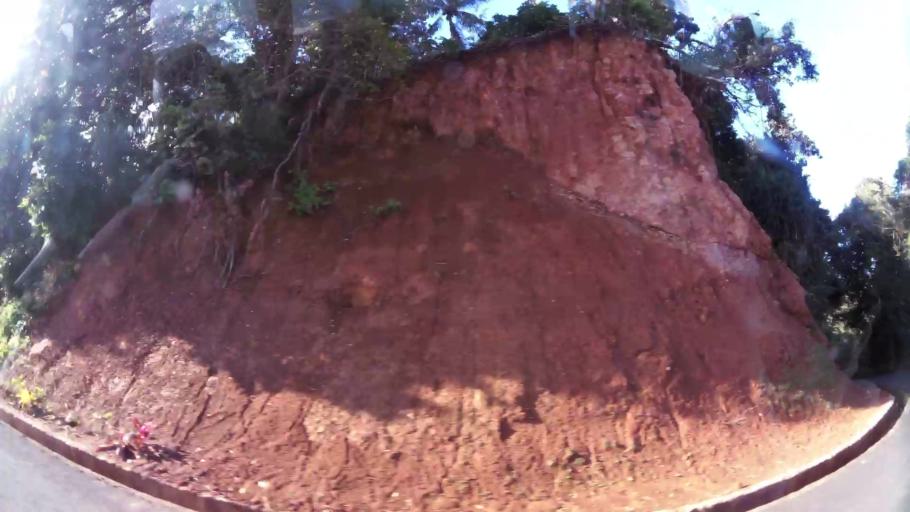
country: DM
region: Saint Andrew
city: Calibishie
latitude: 15.5930
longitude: -61.3565
